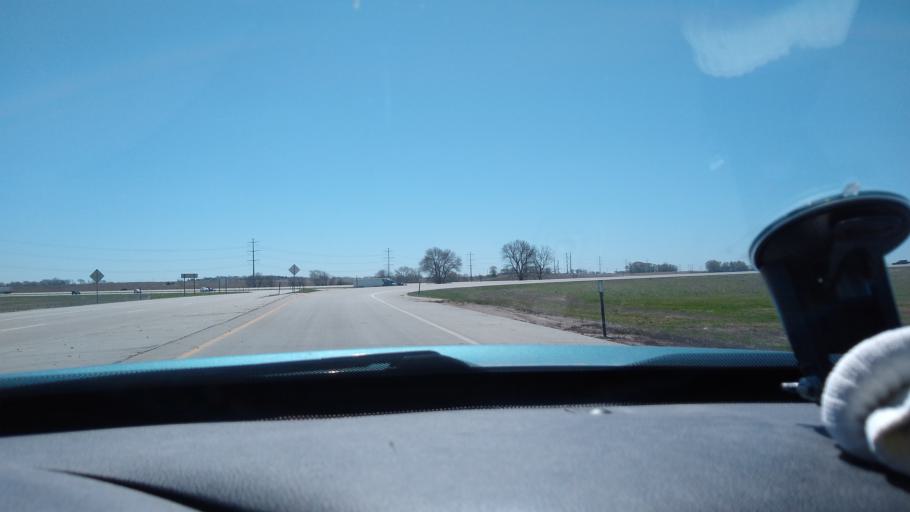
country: US
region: Nebraska
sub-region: Lancaster County
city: Waverly
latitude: 40.8964
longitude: -96.5639
